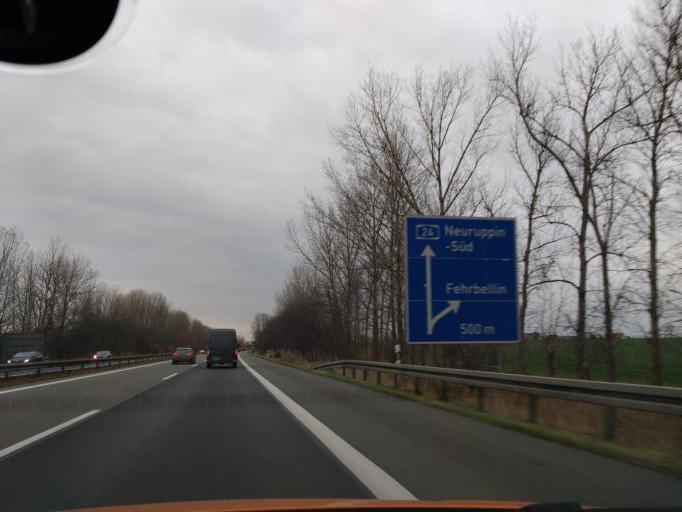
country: DE
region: Brandenburg
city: Fehrbellin
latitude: 52.7966
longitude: 12.7957
